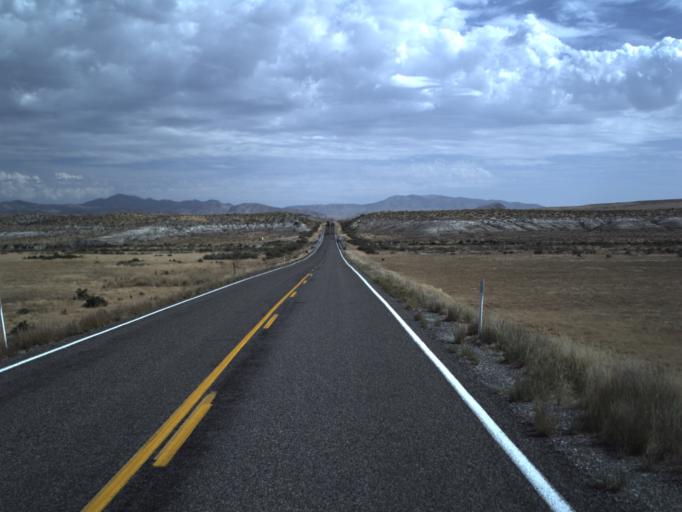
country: US
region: Utah
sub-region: Tooele County
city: Wendover
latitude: 41.4055
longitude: -113.9402
